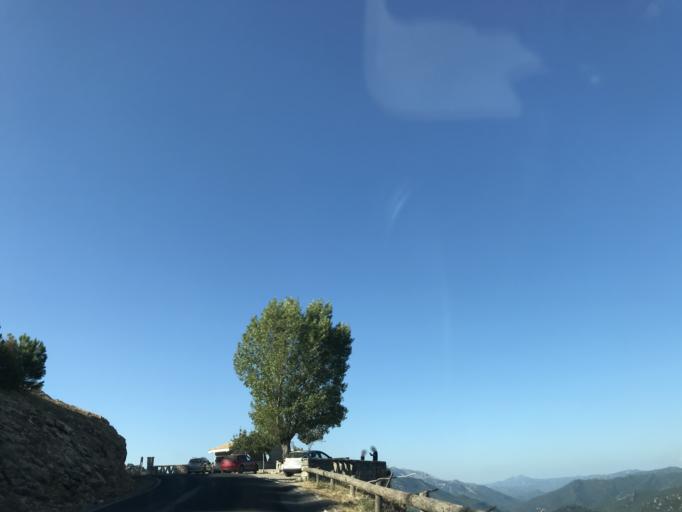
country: ES
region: Andalusia
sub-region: Provincia de Jaen
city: La Iruela
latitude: 37.9403
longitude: -2.9393
